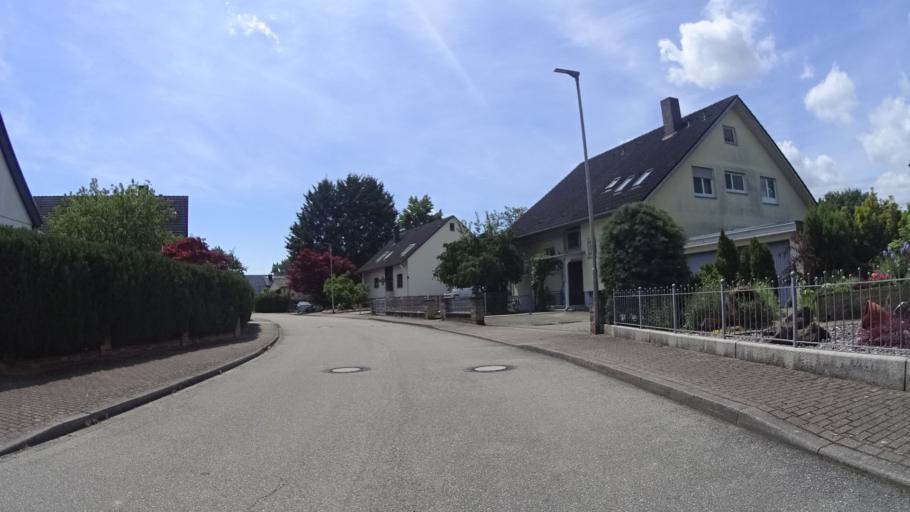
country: DE
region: Baden-Wuerttemberg
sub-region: Freiburg Region
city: Schwanau
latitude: 48.3539
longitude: 7.7535
